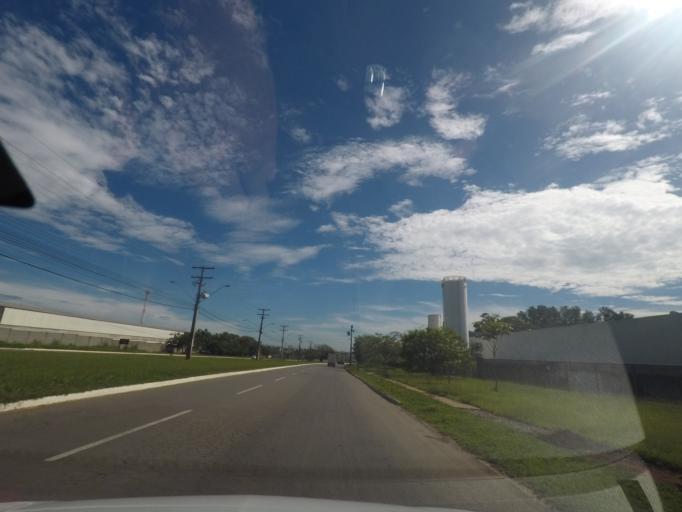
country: BR
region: Goias
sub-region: Aparecida De Goiania
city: Aparecida de Goiania
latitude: -16.7930
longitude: -49.2534
